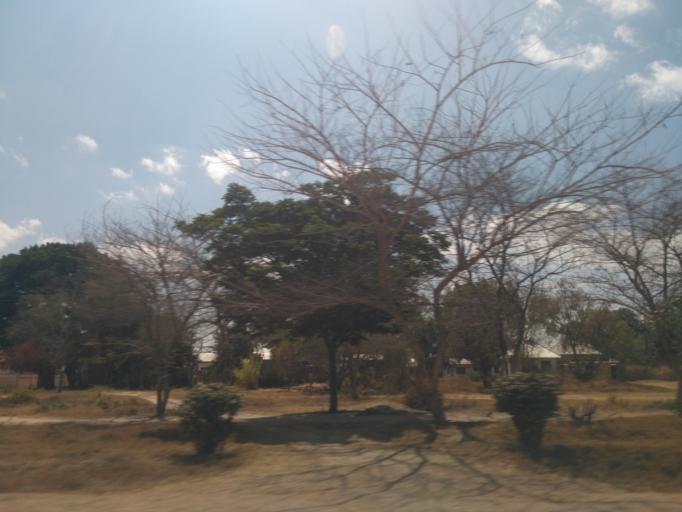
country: TZ
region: Dodoma
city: Dodoma
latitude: -6.1623
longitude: 35.7467
